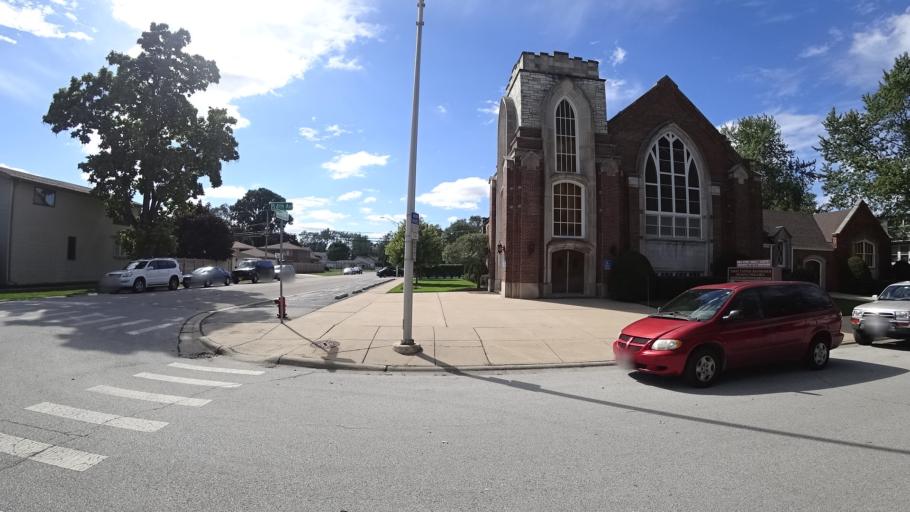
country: US
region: Illinois
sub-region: Cook County
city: Oak Lawn
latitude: 41.7217
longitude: -87.7555
